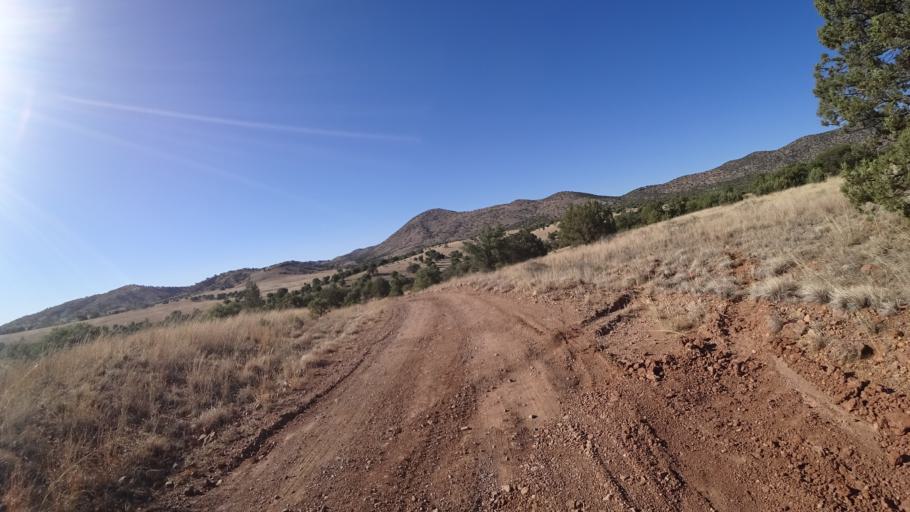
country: MX
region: Sonora
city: Santa Cruz
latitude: 31.4829
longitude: -110.5687
